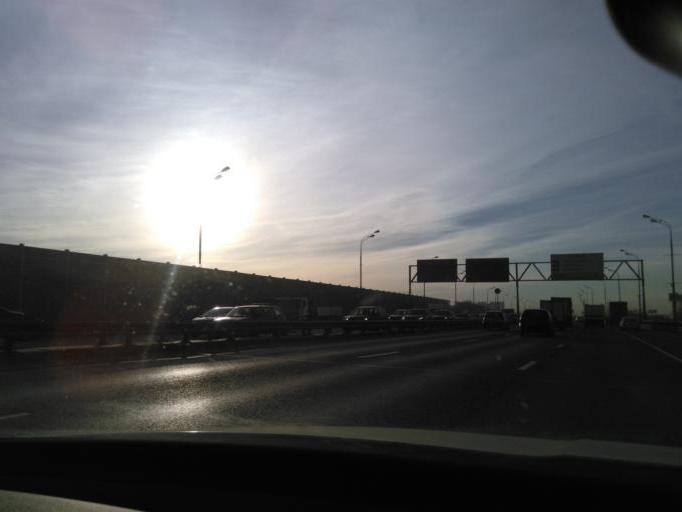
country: RU
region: Moscow
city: Lefortovo
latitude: 55.7326
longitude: 37.7027
